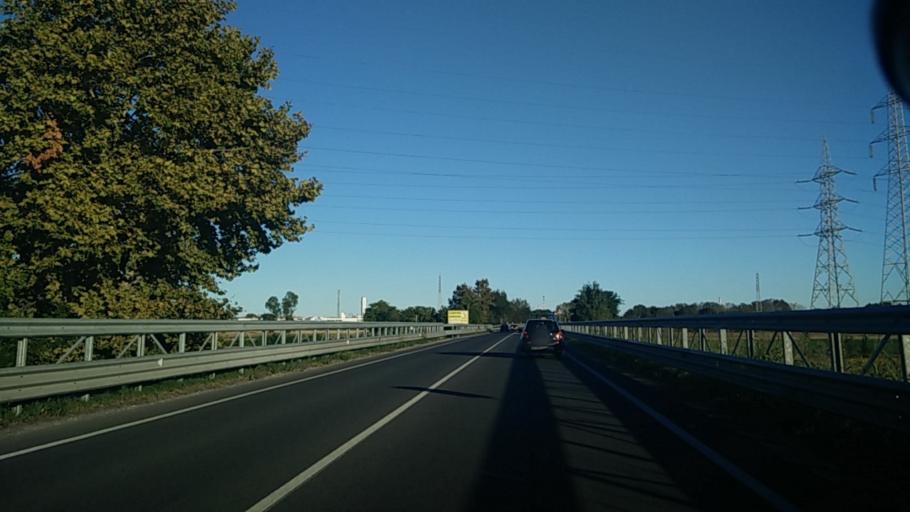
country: IT
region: Veneto
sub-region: Provincia di Venezia
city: Fornase
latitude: 45.4533
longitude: 12.2002
